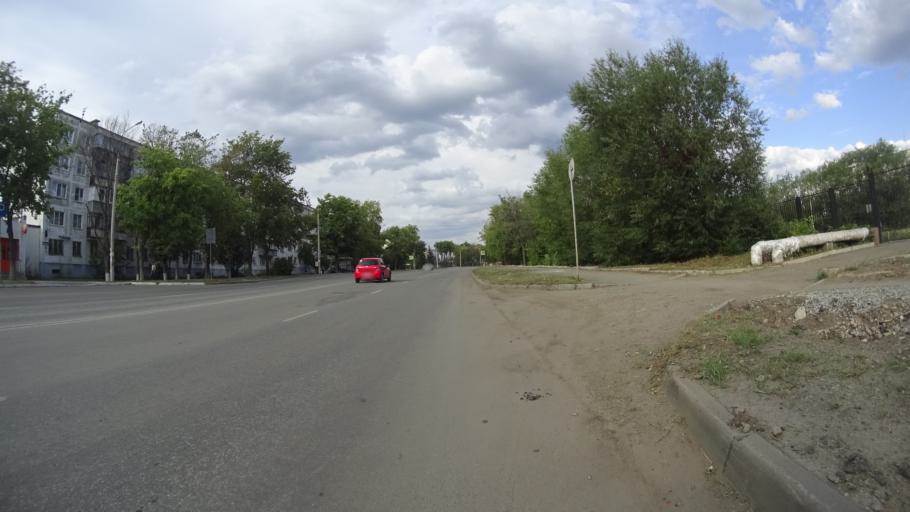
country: RU
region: Chelyabinsk
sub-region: Gorod Chelyabinsk
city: Chelyabinsk
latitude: 55.2014
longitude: 61.3204
